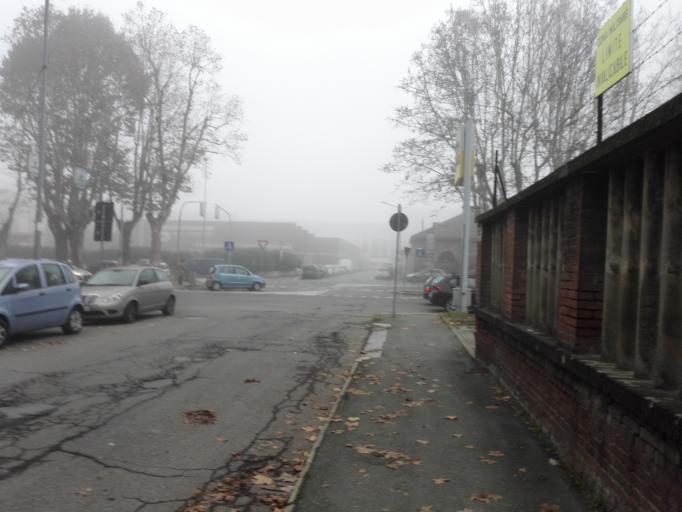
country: IT
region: Piedmont
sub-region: Provincia di Alessandria
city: Alessandria
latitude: 44.9073
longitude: 8.6179
